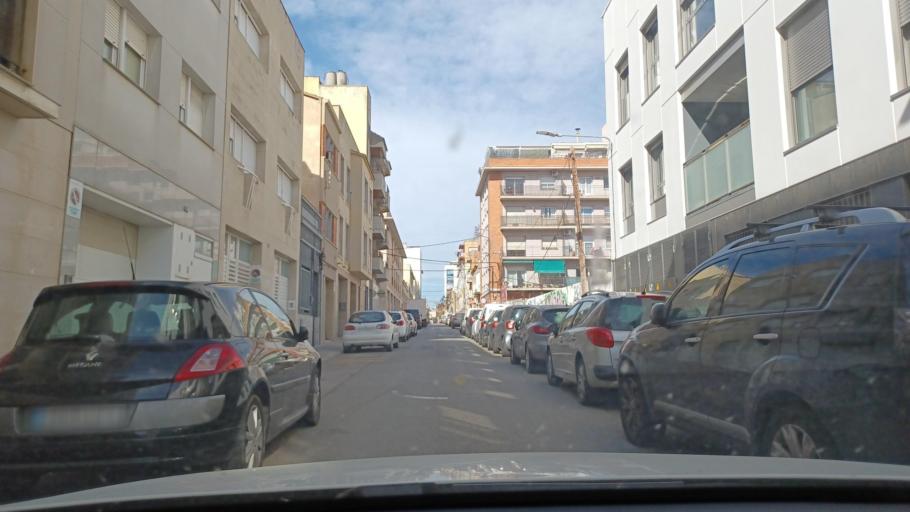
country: ES
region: Catalonia
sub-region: Provincia de Barcelona
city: Sabadell
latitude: 41.5375
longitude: 2.1146
